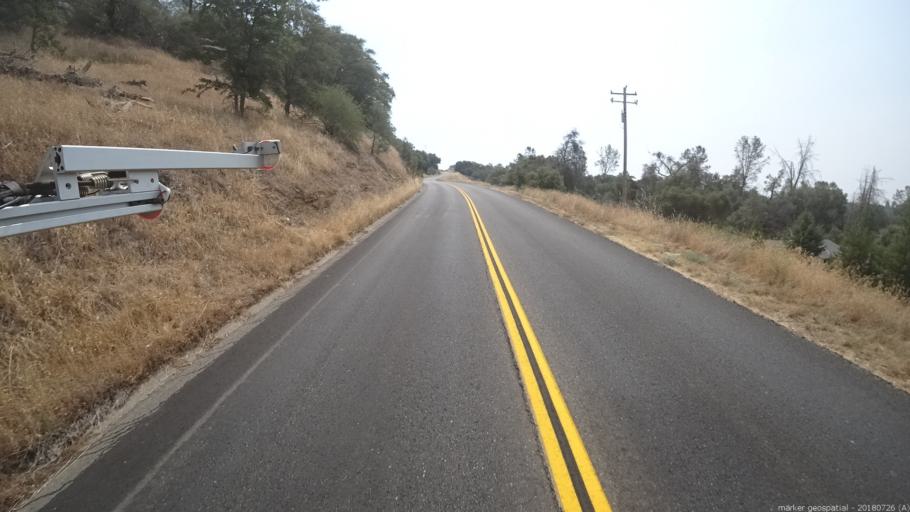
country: US
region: California
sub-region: Madera County
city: Coarsegold
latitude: 37.2513
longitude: -119.7025
